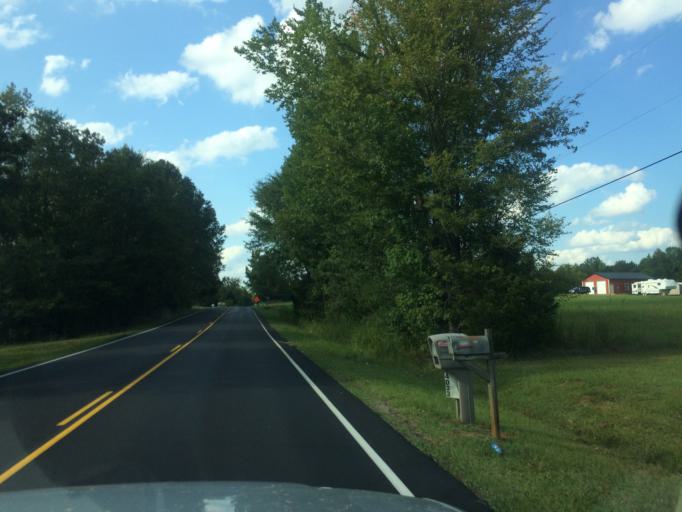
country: US
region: South Carolina
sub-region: Greenwood County
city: Ware Shoals
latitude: 34.4705
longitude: -82.1606
